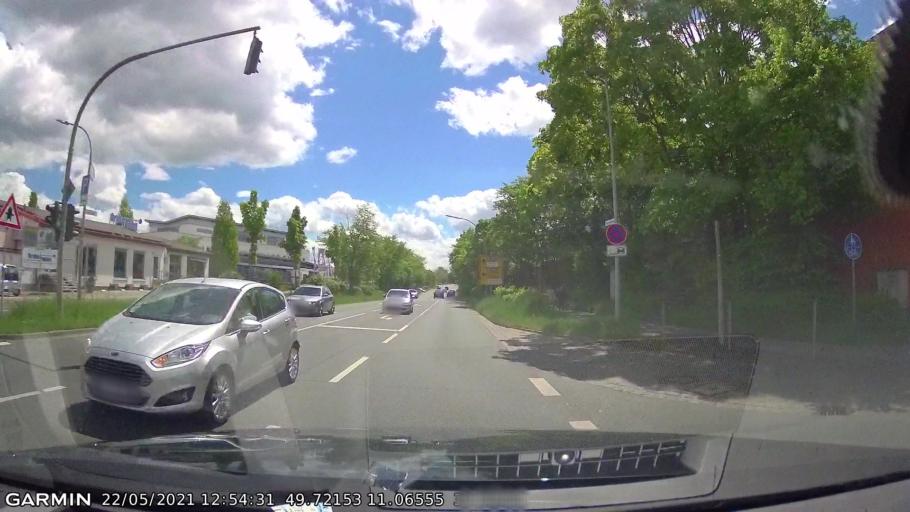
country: DE
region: Bavaria
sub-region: Upper Franconia
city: Forchheim
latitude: 49.7215
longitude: 11.0656
